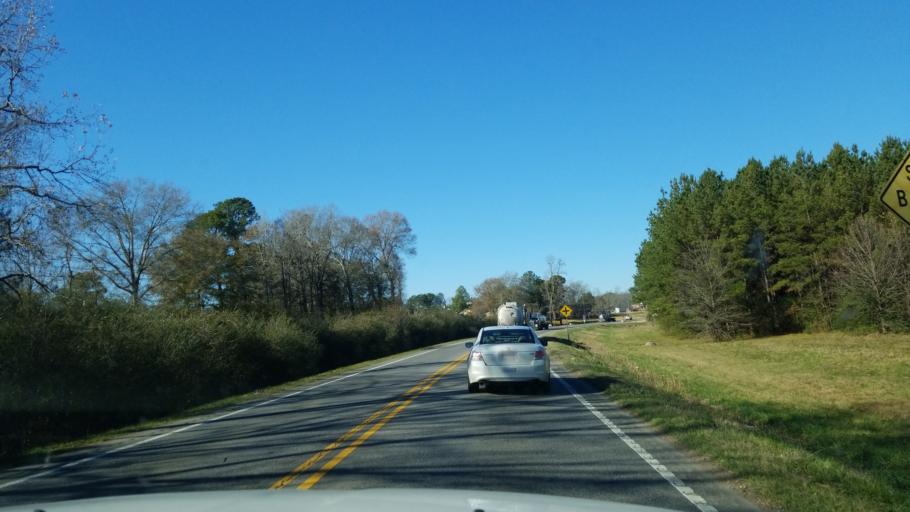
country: US
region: Alabama
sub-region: Pickens County
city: Gordo
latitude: 33.3182
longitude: -87.9069
